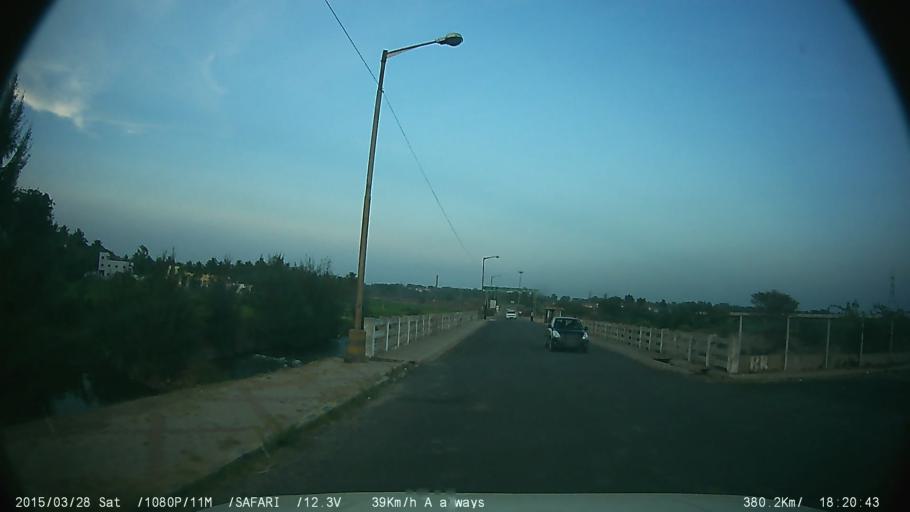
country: IN
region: Karnataka
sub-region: Mandya
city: Shrirangapattana
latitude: 12.4252
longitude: 76.5793
